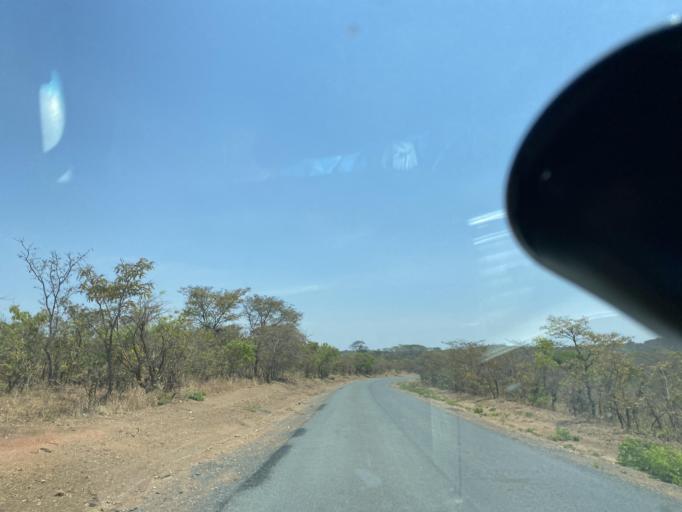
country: ZM
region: Lusaka
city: Kafue
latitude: -15.8671
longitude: 28.4314
